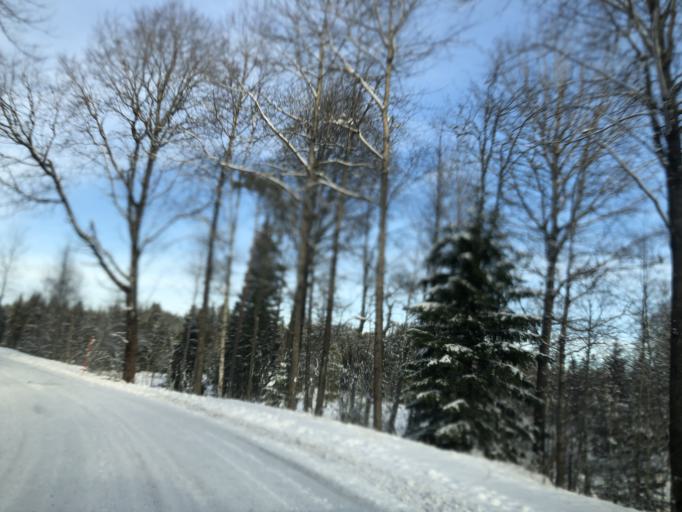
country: SE
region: Vaestra Goetaland
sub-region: Ulricehamns Kommun
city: Ulricehamn
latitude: 57.7707
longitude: 13.5235
